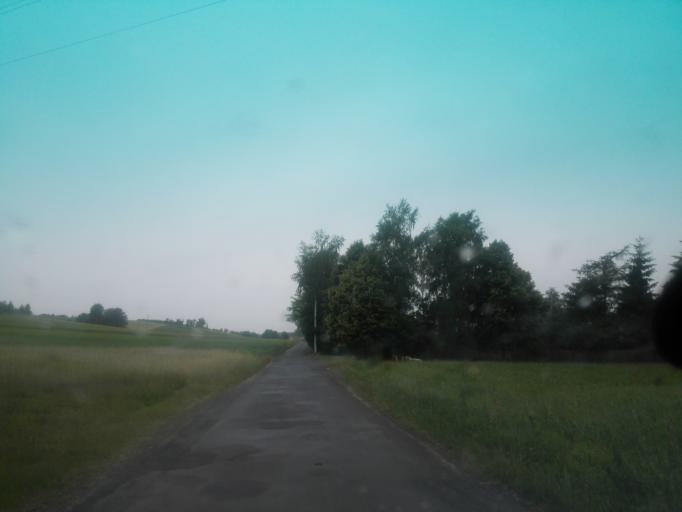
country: PL
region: Silesian Voivodeship
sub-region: Powiat czestochowski
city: Mstow
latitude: 50.8275
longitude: 19.3207
